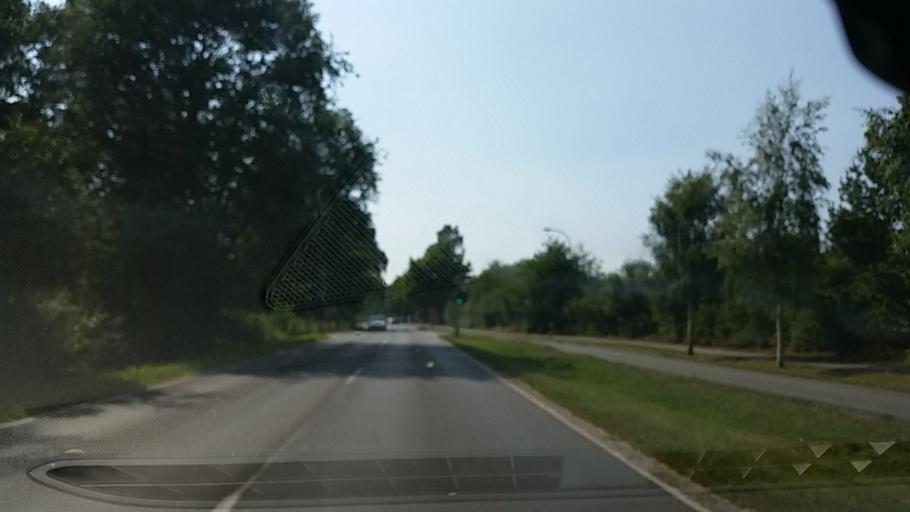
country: DE
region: Schleswig-Holstein
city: Oststeinbek
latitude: 53.5424
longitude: 10.1813
